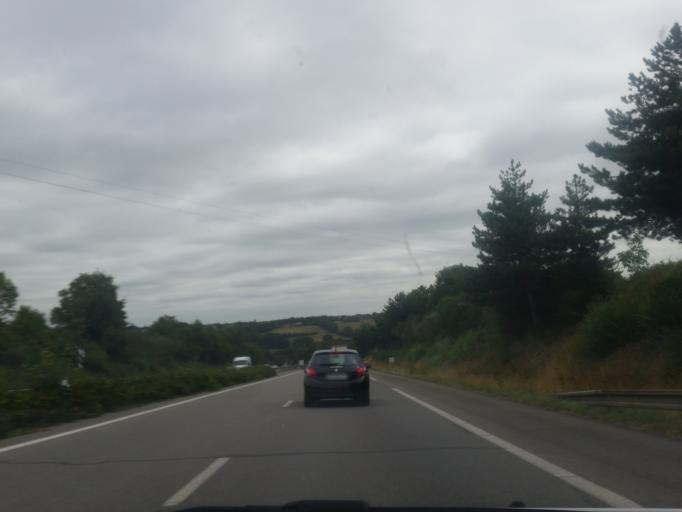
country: FR
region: Pays de la Loire
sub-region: Departement de la Loire-Atlantique
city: Mauves-sur-Loire
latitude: 47.3054
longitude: -1.4225
